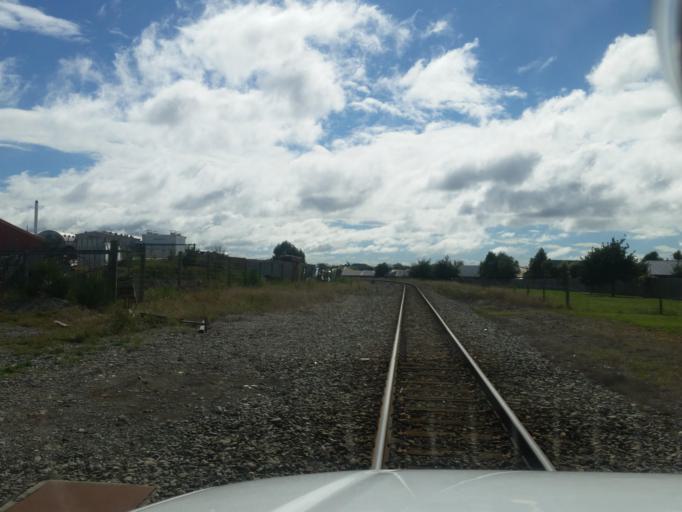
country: NZ
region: Canterbury
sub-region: Waimakariri District
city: Kaiapoi
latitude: -43.3921
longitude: 172.6573
